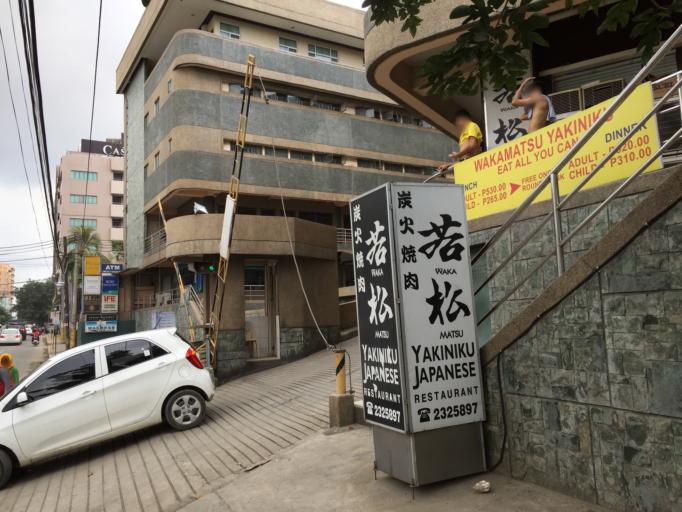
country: PH
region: Central Visayas
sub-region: Cebu City
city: Baugo
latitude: 10.3221
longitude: 123.9130
